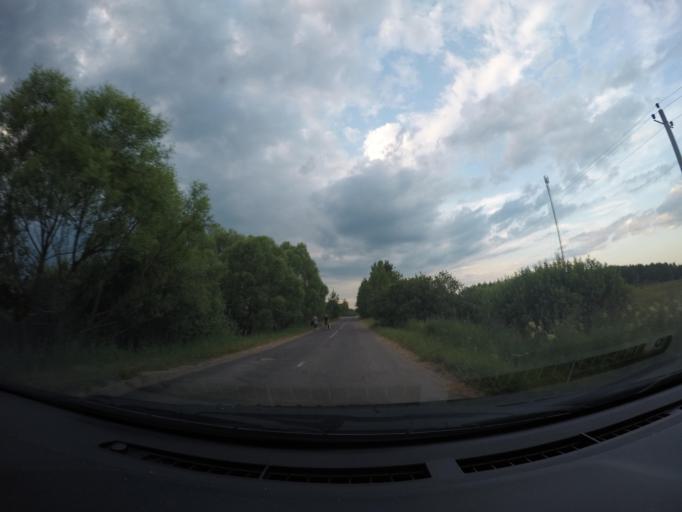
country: RU
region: Moskovskaya
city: Krasnyy Tkach
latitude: 55.4265
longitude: 39.2437
